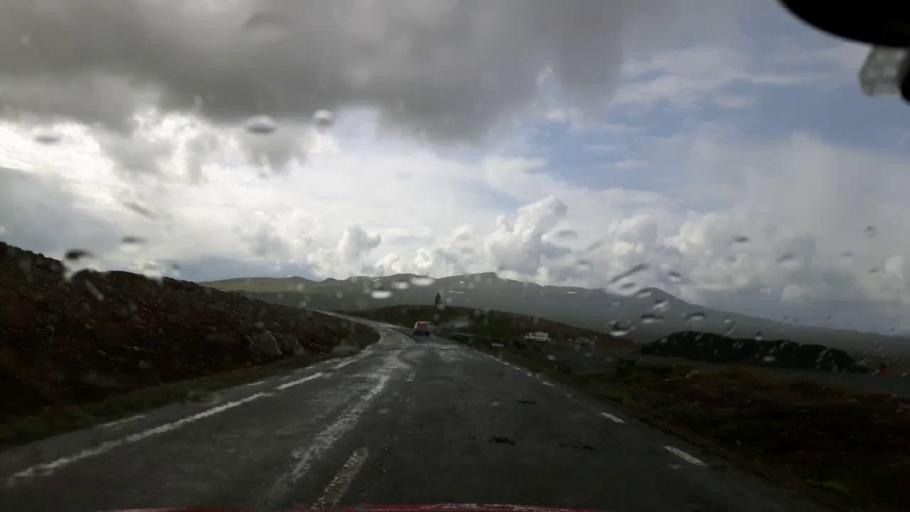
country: NO
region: Nordland
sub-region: Hattfjelldal
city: Hattfjelldal
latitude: 65.0907
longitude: 14.4604
